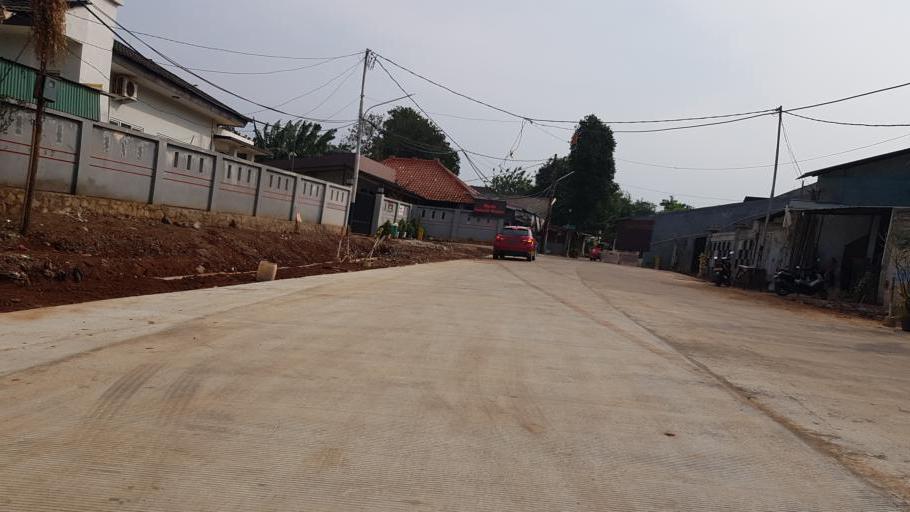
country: ID
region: West Java
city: Pamulang
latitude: -6.3257
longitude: 106.8012
